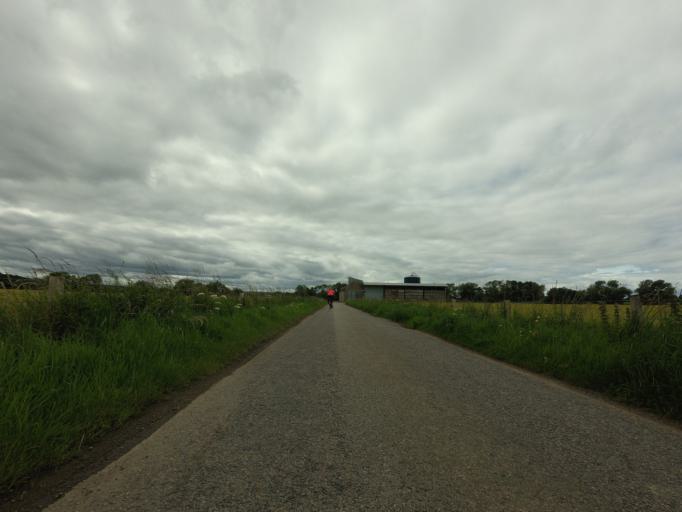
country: GB
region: Scotland
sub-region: Moray
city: Forres
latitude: 57.6263
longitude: -3.6056
